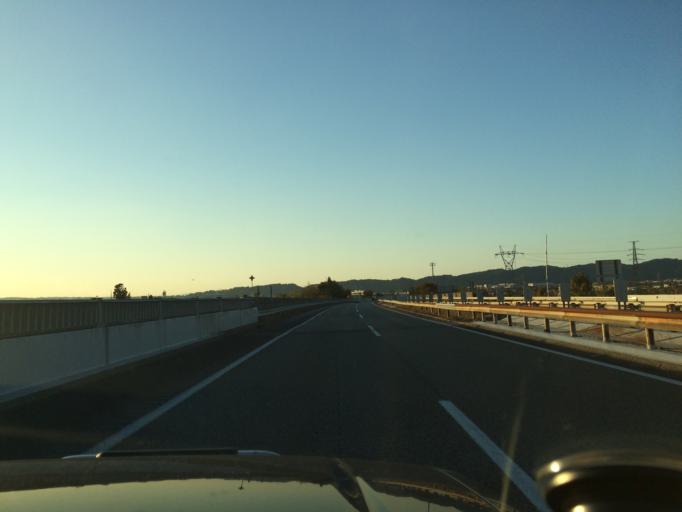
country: JP
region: Toyama
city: Toyama-shi
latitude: 36.6651
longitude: 137.1873
